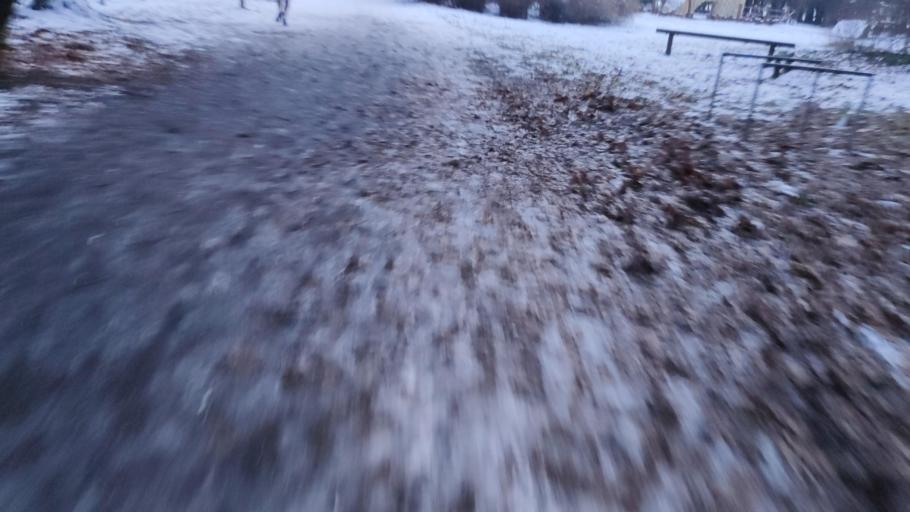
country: PL
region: Lower Silesian Voivodeship
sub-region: Powiat wroclawski
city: Bielany Wroclawskie
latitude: 51.0852
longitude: 16.9769
